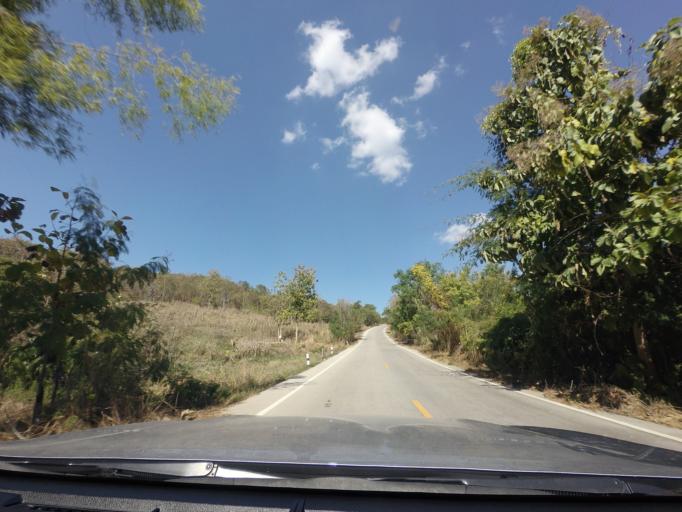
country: TH
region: Lampang
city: Chae Hom
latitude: 18.5690
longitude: 99.6249
